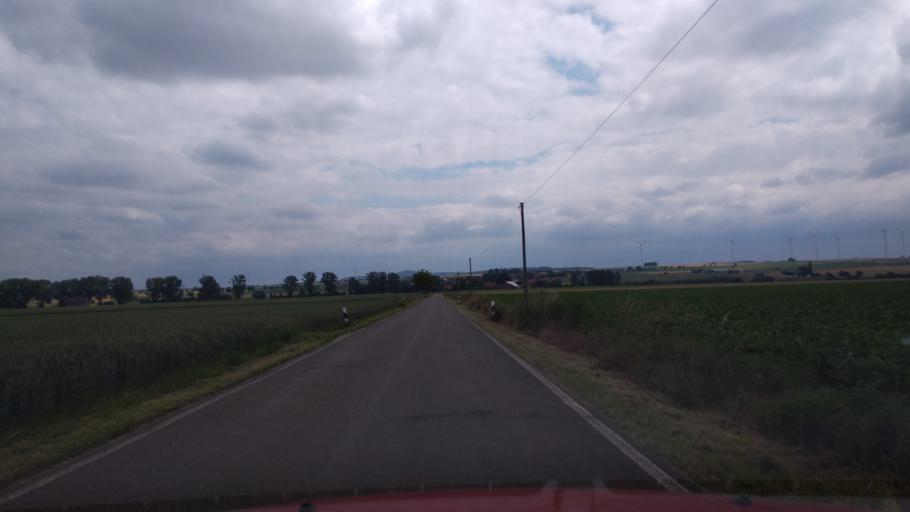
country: DE
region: North Rhine-Westphalia
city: Borgentreich
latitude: 51.5262
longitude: 9.2206
